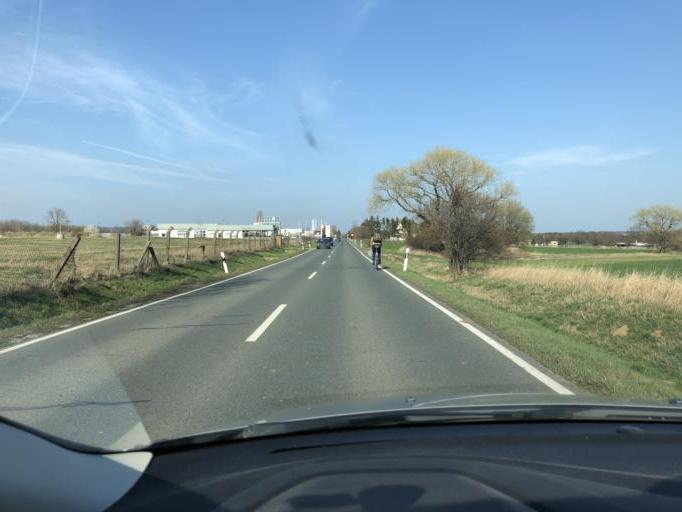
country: DE
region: Thuringia
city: Weimar
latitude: 50.9608
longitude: 11.3089
